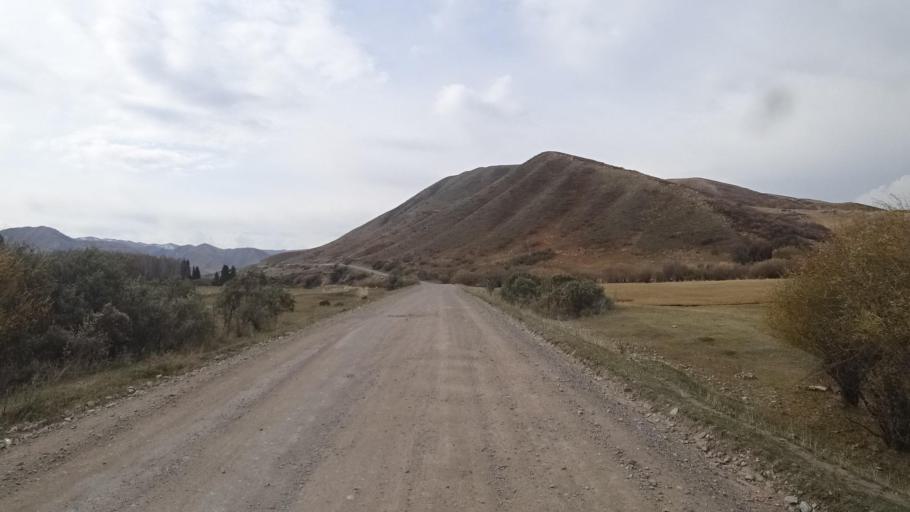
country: KG
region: Ysyk-Koel
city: Teploklyuchenka
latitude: 42.7356
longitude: 78.8323
